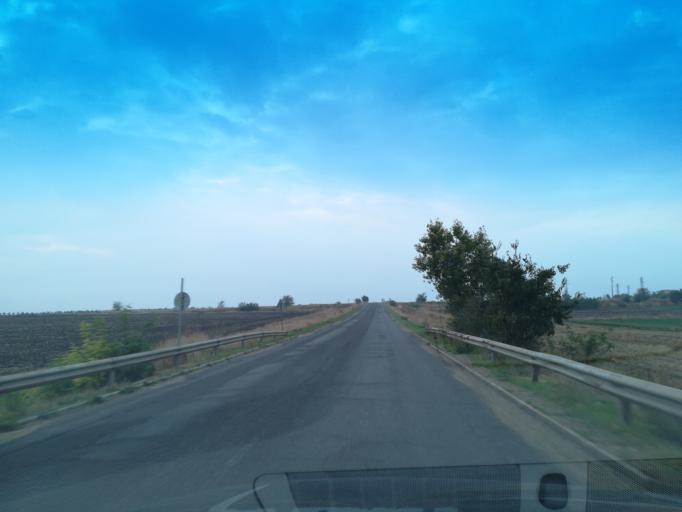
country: BG
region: Stara Zagora
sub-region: Obshtina Chirpan
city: Chirpan
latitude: 42.1919
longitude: 25.3170
